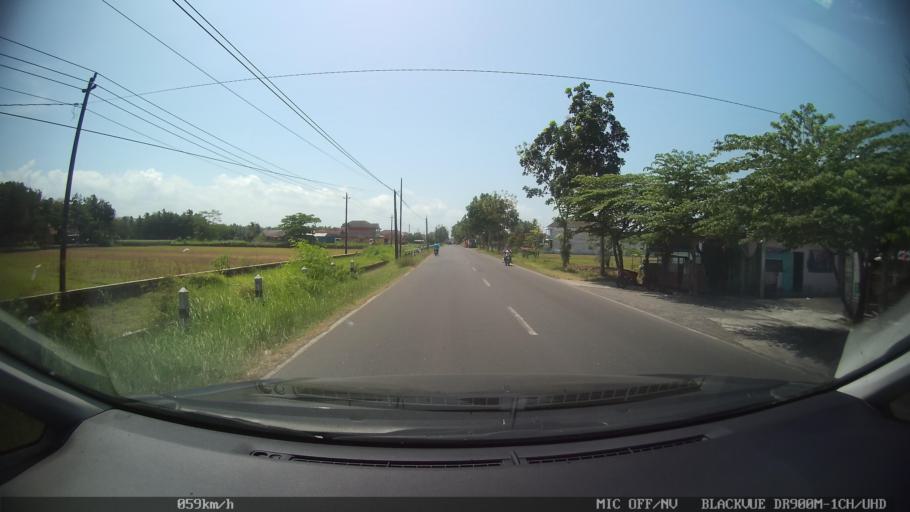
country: ID
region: Daerah Istimewa Yogyakarta
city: Srandakan
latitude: -7.9521
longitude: 110.2017
